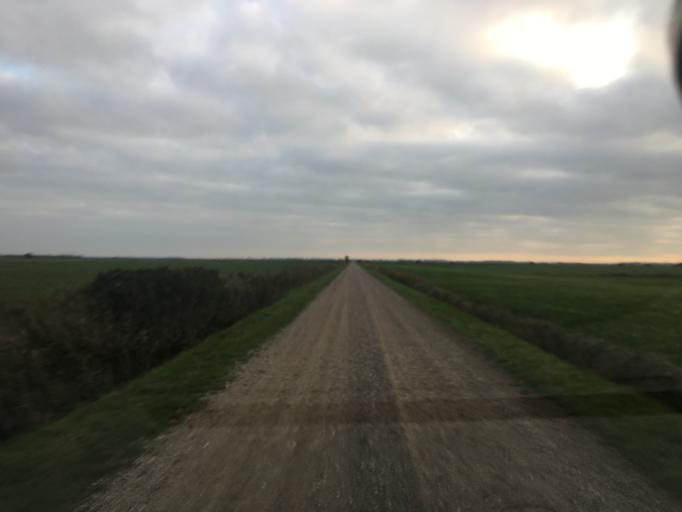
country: DE
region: Schleswig-Holstein
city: Aventoft
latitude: 54.9368
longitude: 8.7775
